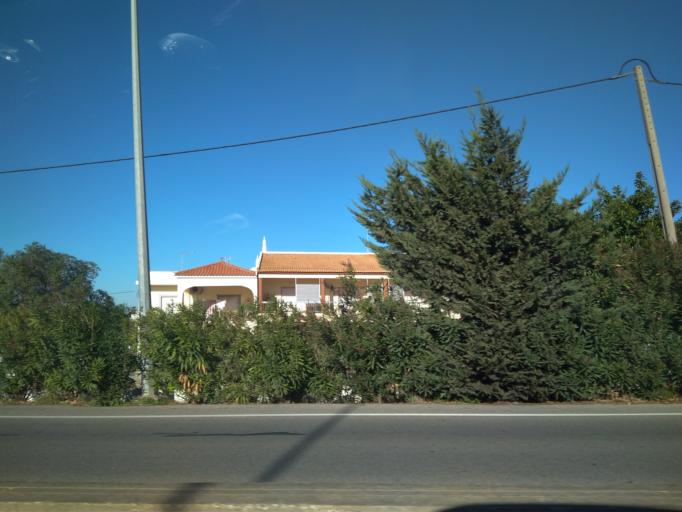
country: PT
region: Faro
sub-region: Faro
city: Faro
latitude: 37.0314
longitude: -7.9673
